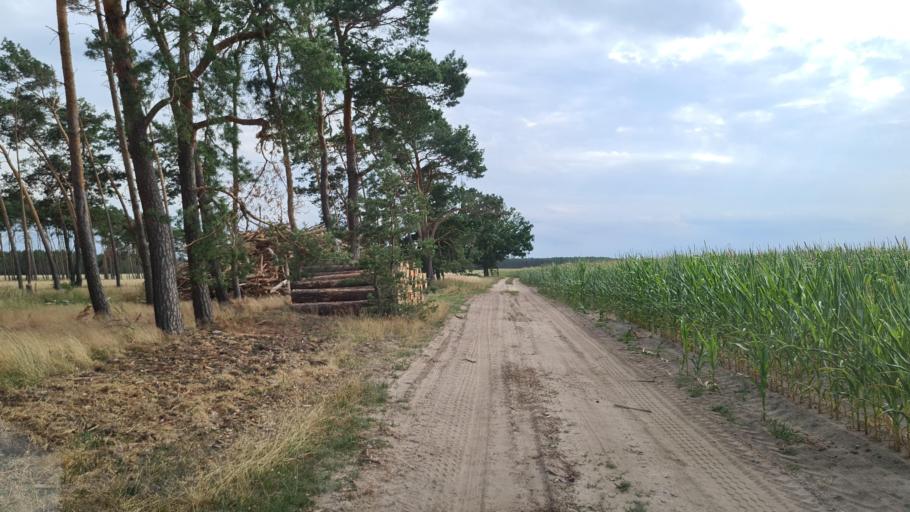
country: DE
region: Saxony-Anhalt
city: Holzdorf
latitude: 51.8238
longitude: 13.1974
